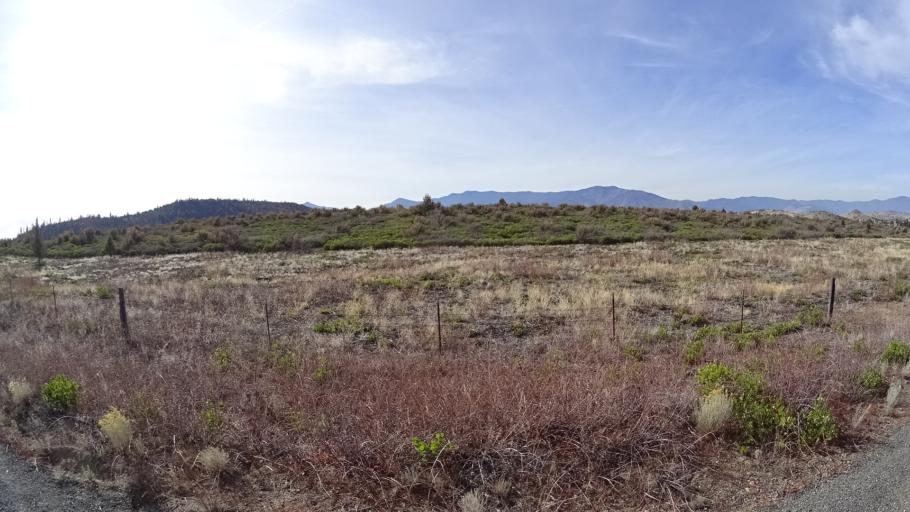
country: US
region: California
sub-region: Siskiyou County
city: Weed
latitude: 41.4827
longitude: -122.3644
